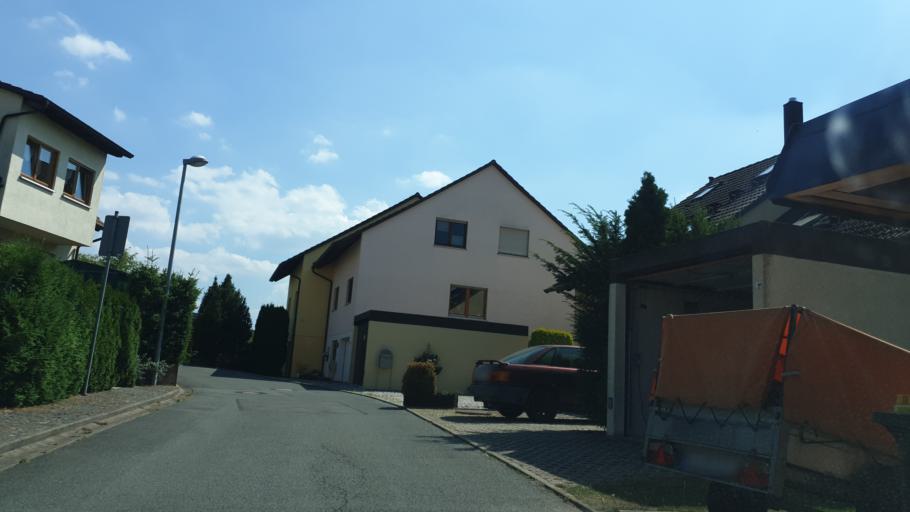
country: DE
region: Saxony
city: Gersdorf
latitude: 50.7477
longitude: 12.7127
